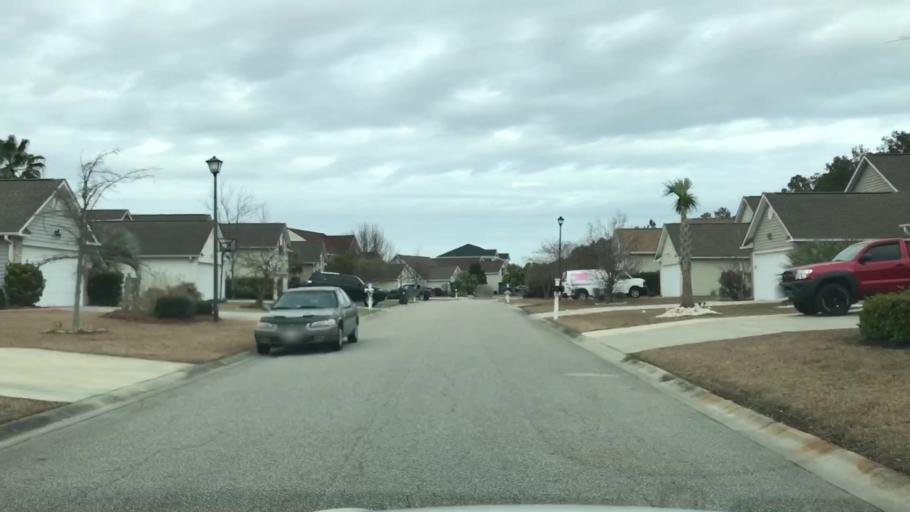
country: US
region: South Carolina
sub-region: Horry County
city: Socastee
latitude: 33.6709
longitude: -78.9722
